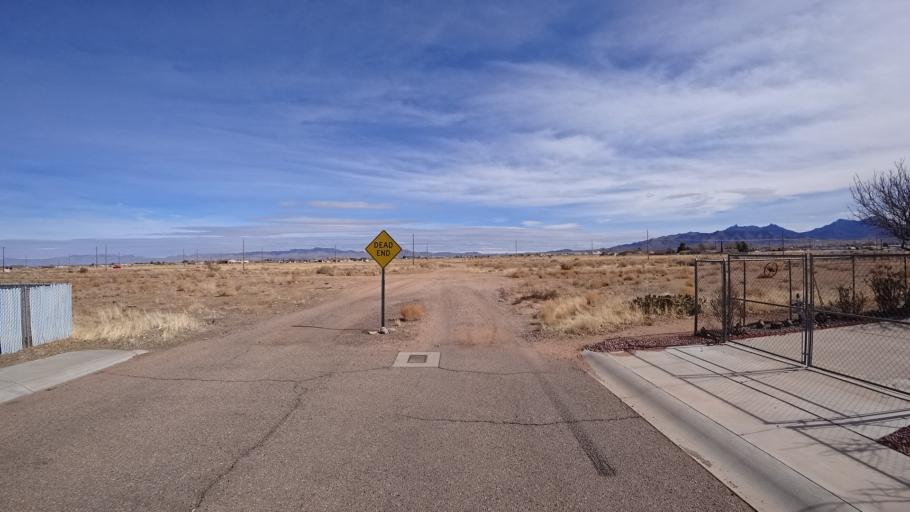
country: US
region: Arizona
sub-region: Mohave County
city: New Kingman-Butler
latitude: 35.2302
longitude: -114.0180
